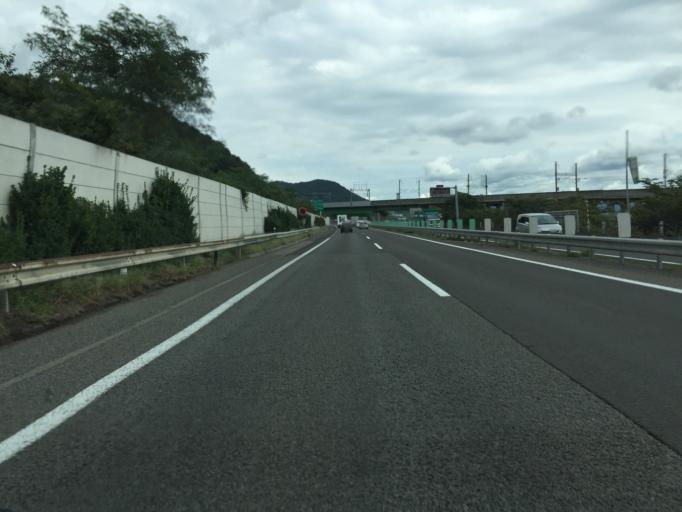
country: JP
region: Fukushima
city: Hobaramachi
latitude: 37.8820
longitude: 140.5359
